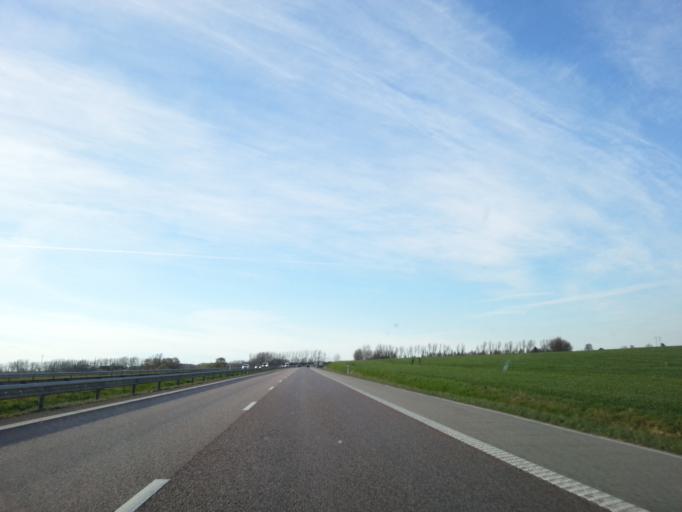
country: SE
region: Skane
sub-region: Helsingborg
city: Gantofta
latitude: 55.9809
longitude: 12.7847
